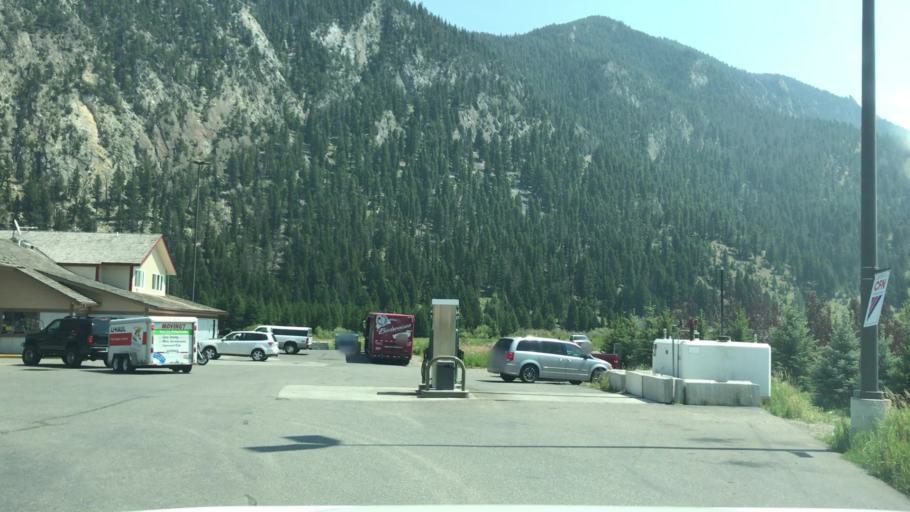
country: US
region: Montana
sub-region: Gallatin County
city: Big Sky
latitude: 45.2591
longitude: -111.2543
